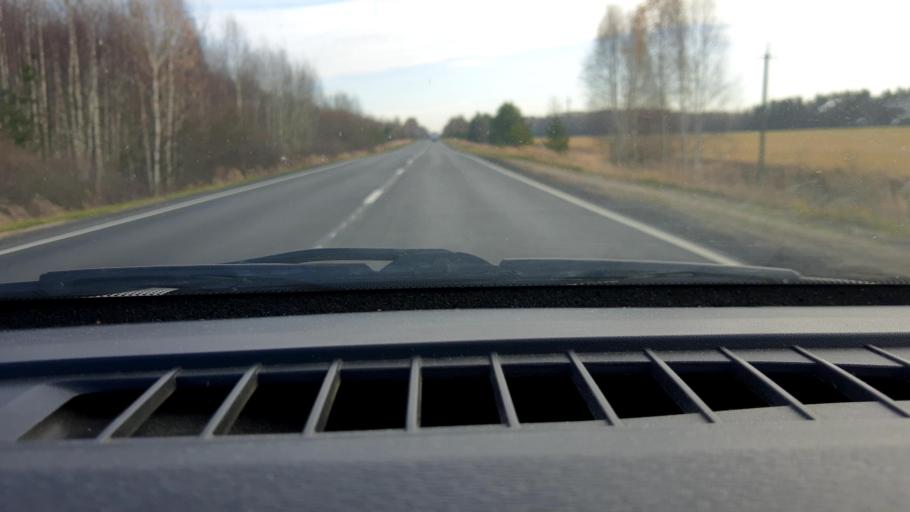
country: RU
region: Nizjnij Novgorod
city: Novaya Balakhna
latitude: 56.5945
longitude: 43.6506
